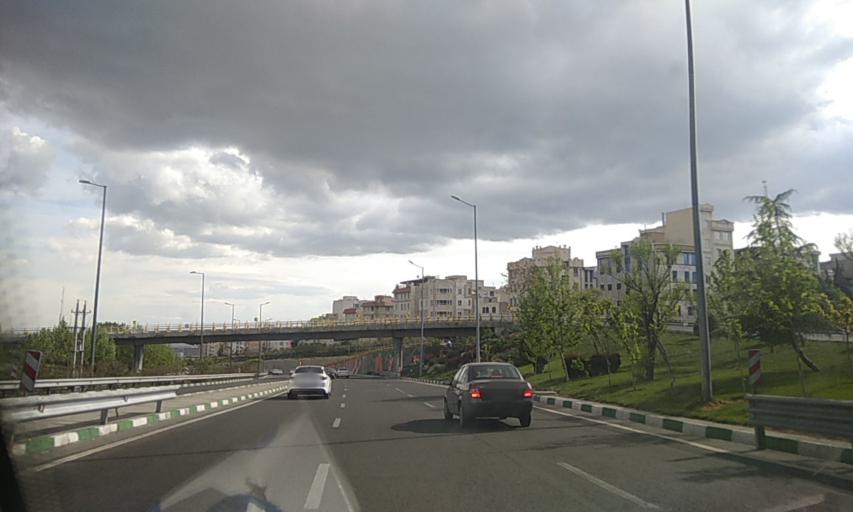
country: IR
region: Tehran
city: Tajrish
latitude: 35.7635
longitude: 51.2967
